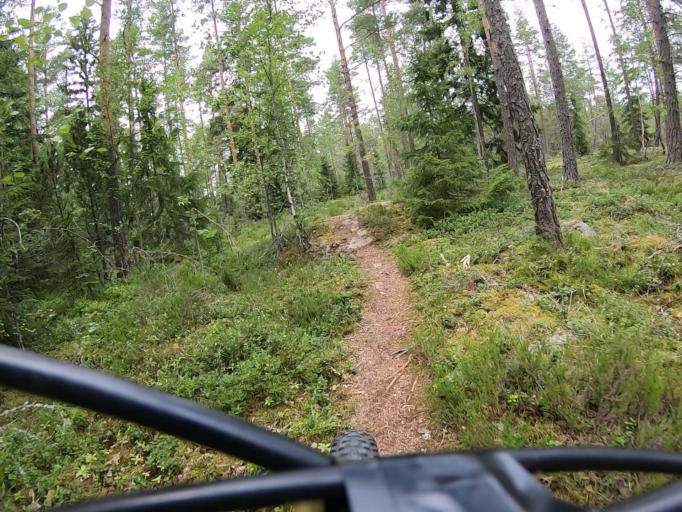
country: FI
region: Varsinais-Suomi
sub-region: Vakka-Suomi
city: Uusikaupunki
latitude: 60.8368
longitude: 21.3962
